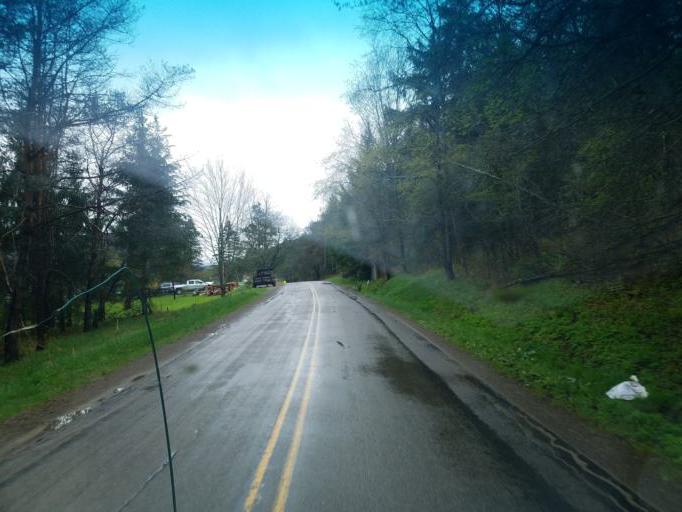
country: US
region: New York
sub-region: Allegany County
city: Wellsville
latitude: 41.9643
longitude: -77.8470
